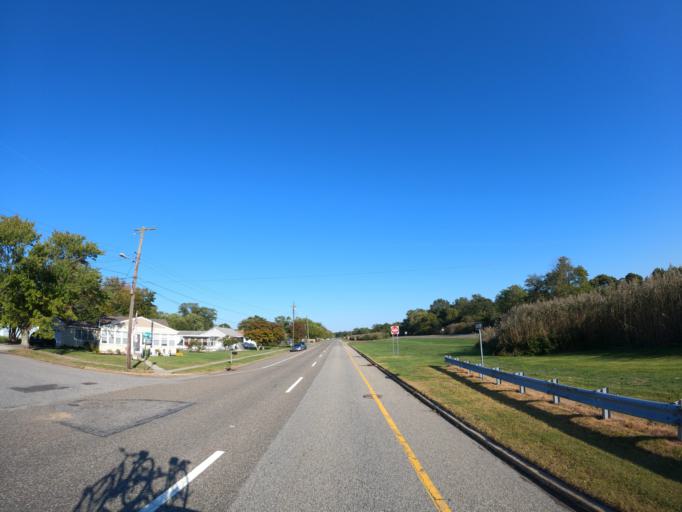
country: US
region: New Jersey
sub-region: Cape May County
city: North Cape May
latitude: 38.9735
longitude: -74.9526
